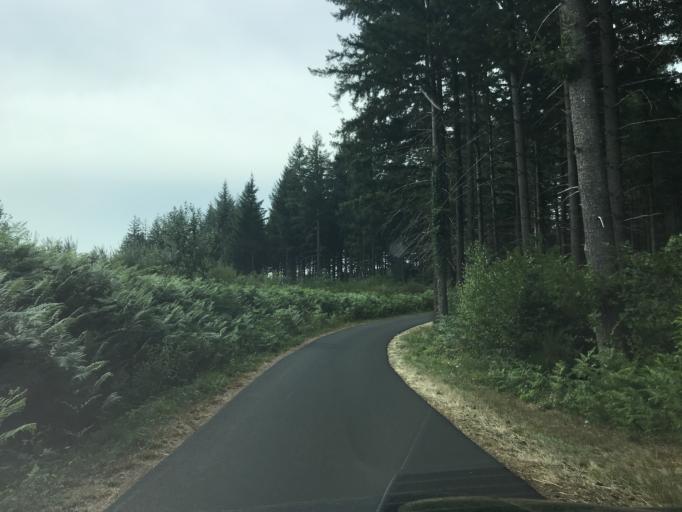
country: FR
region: Limousin
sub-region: Departement de la Correze
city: Neuvic
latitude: 45.3784
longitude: 2.2323
